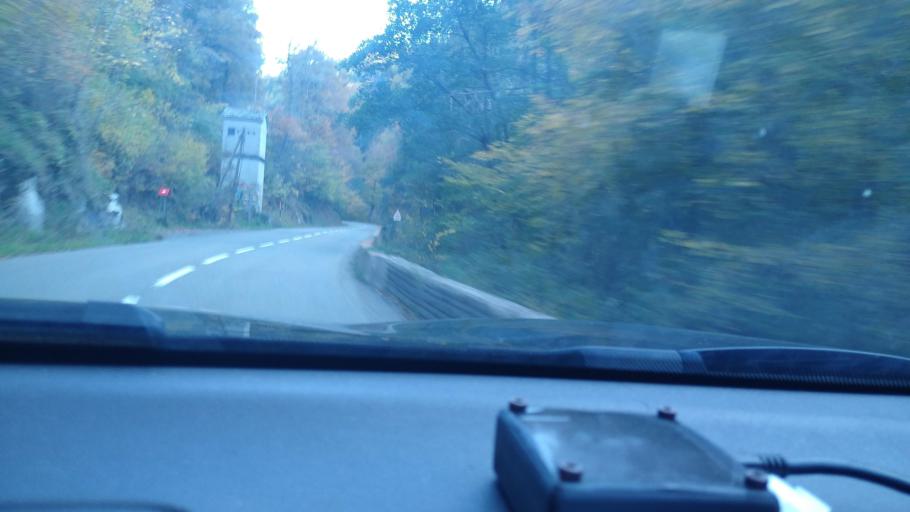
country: FR
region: Languedoc-Roussillon
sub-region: Departement de l'Aude
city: Quillan
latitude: 42.7306
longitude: 2.1039
